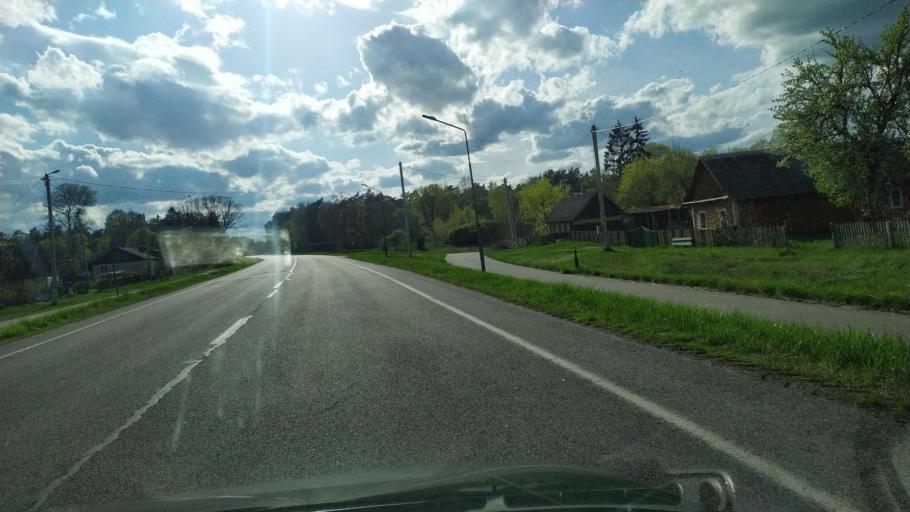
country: BY
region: Brest
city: Pruzhany
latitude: 52.7035
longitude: 24.3169
